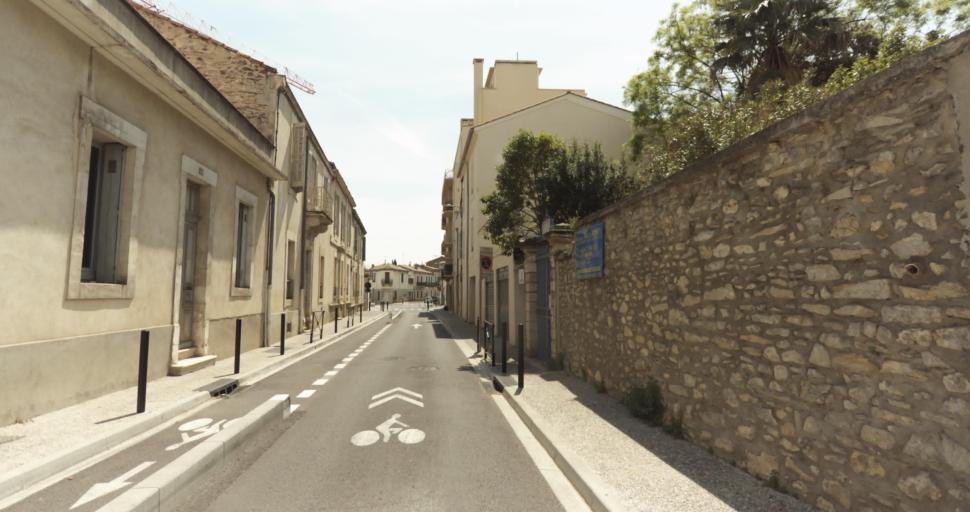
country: FR
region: Languedoc-Roussillon
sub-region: Departement du Gard
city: Nimes
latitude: 43.8455
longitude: 4.3673
